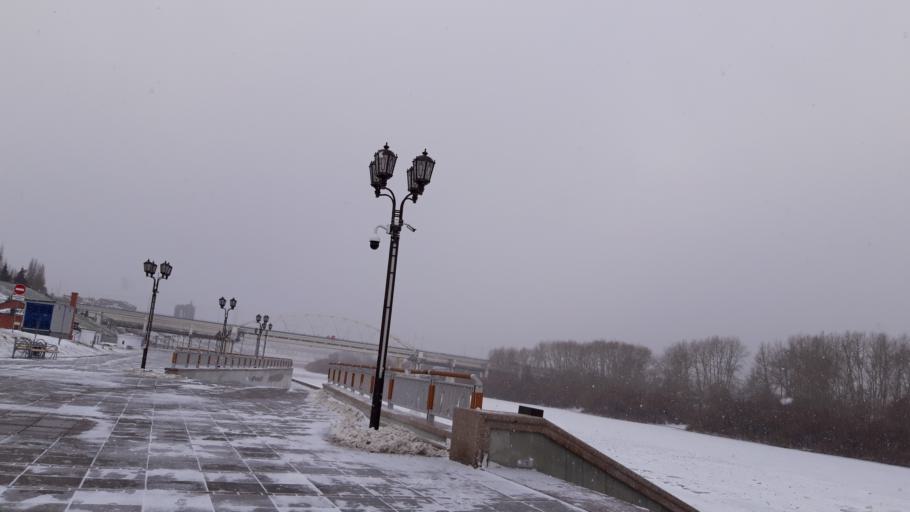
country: RU
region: Tjumen
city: Tyumen
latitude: 57.1620
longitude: 65.5482
